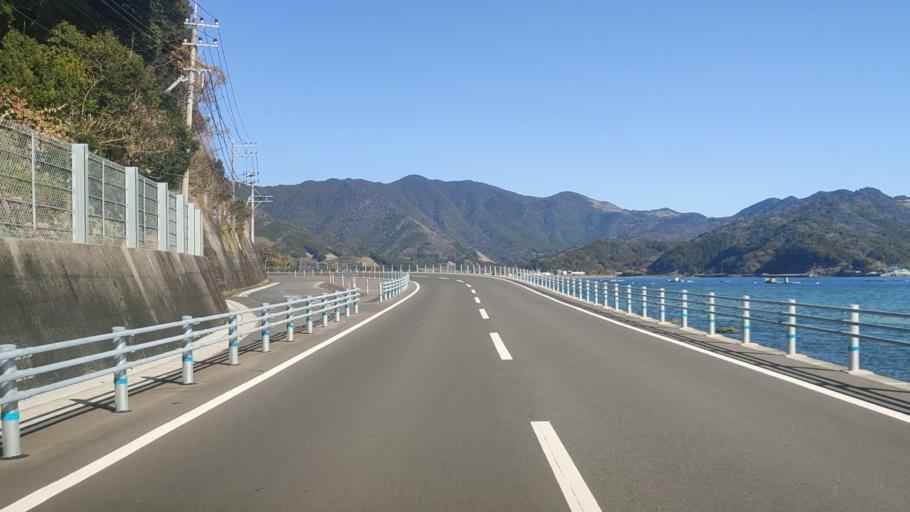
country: JP
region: Oita
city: Saiki
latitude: 32.7947
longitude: 131.8869
